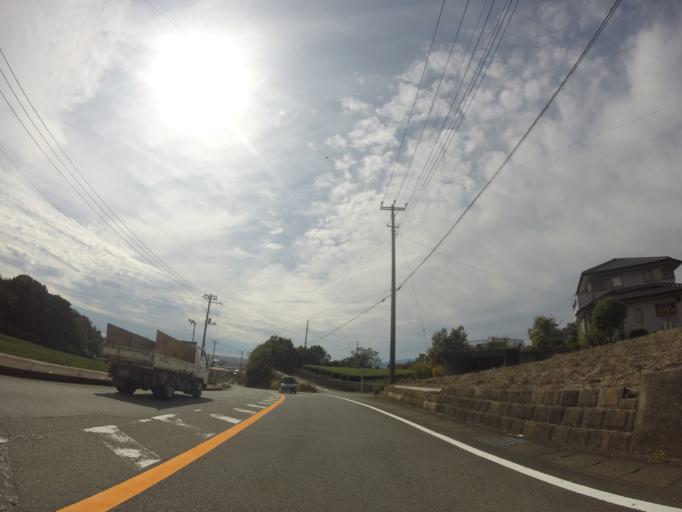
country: JP
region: Shizuoka
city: Fuji
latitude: 35.1928
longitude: 138.6988
